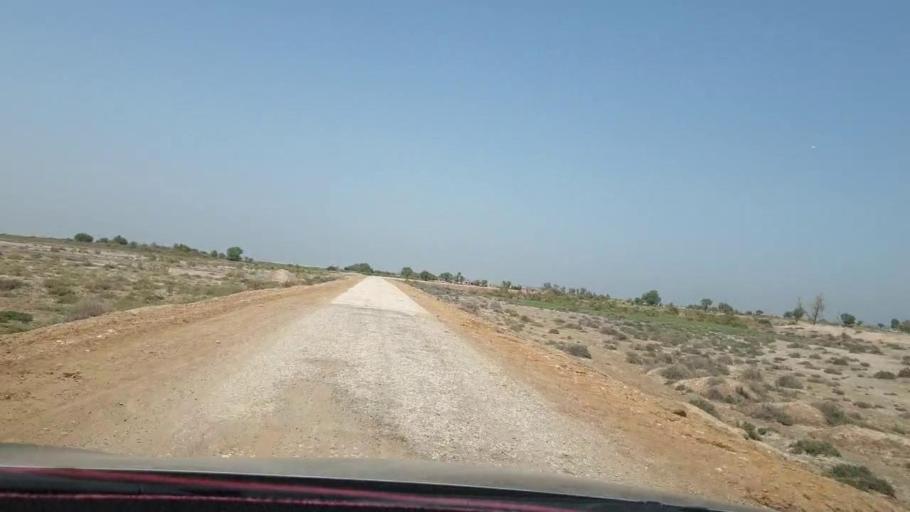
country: PK
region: Sindh
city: Warah
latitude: 27.5211
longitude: 67.7086
